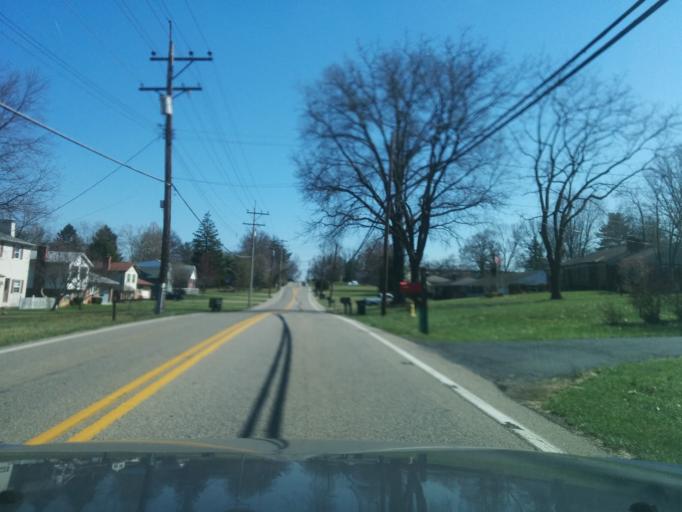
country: US
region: Ohio
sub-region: Hamilton County
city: Groesbeck
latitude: 39.2354
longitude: -84.6015
